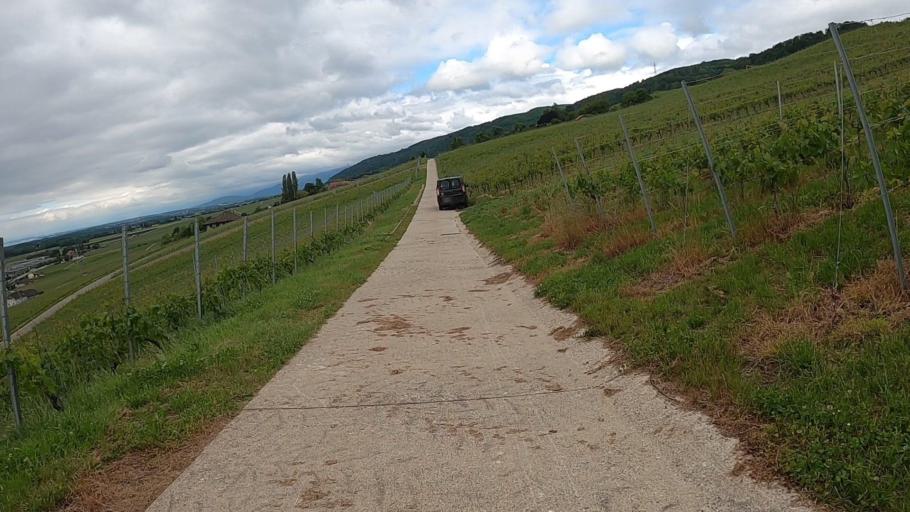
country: CH
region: Vaud
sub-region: Nyon District
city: Rolle
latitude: 46.4706
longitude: 6.3296
